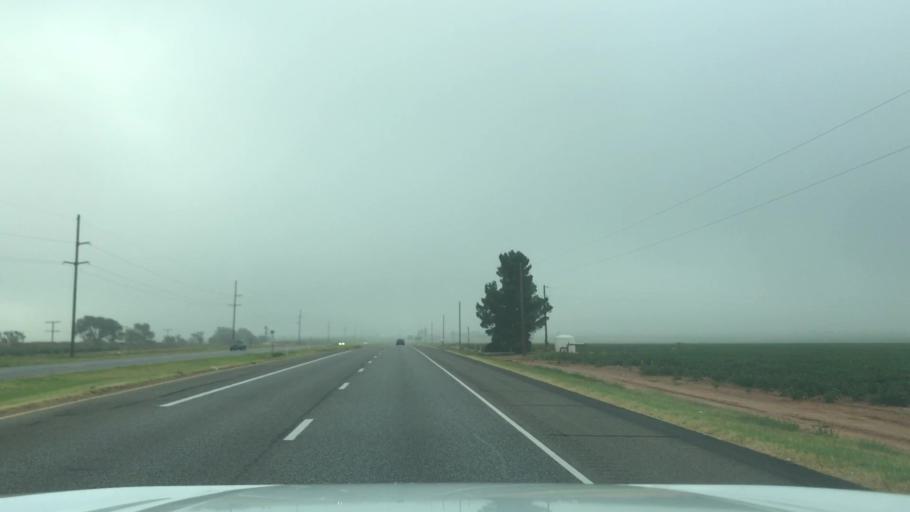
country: US
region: Texas
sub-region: Lubbock County
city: Slaton
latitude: 33.4700
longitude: -101.6884
